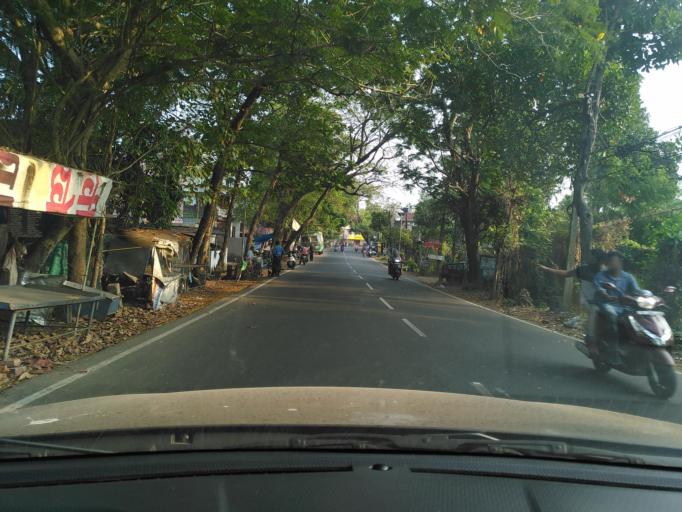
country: IN
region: Kerala
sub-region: Ernakulam
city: Cochin
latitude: 9.8988
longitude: 76.2834
